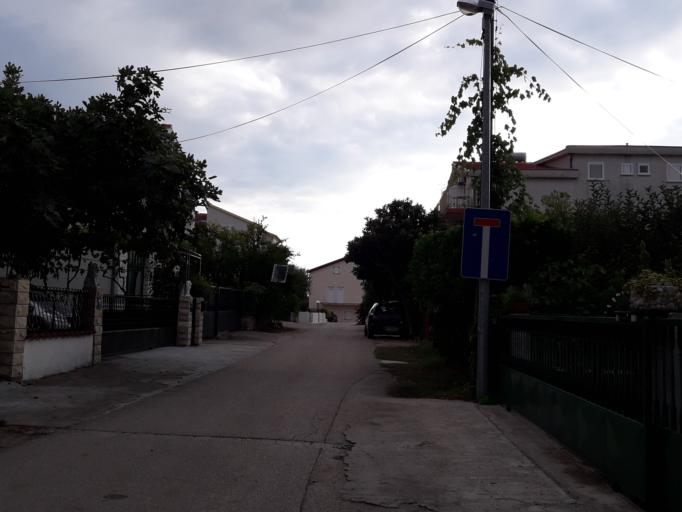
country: HR
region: Sibensko-Kniniska
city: Vodice
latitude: 43.7469
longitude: 15.7993
